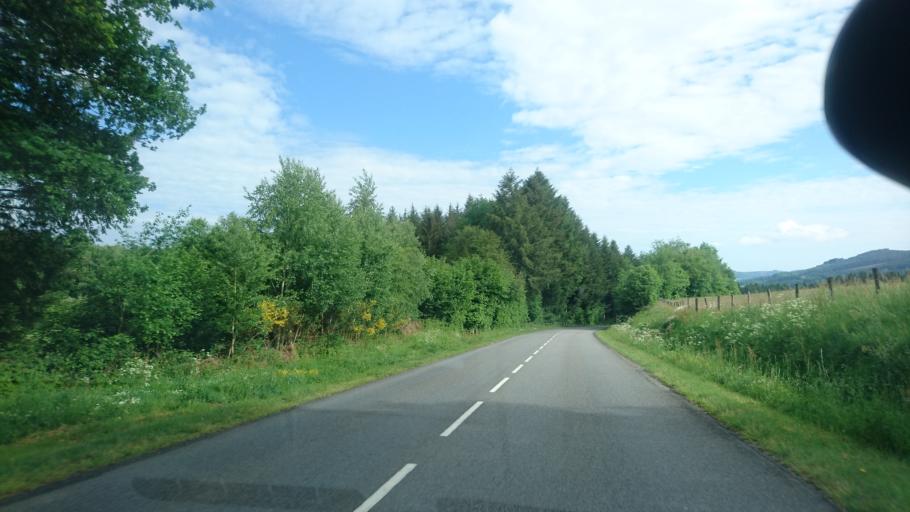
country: FR
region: Limousin
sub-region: Departement de la Haute-Vienne
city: Peyrat-le-Chateau
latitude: 45.7965
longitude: 1.7633
